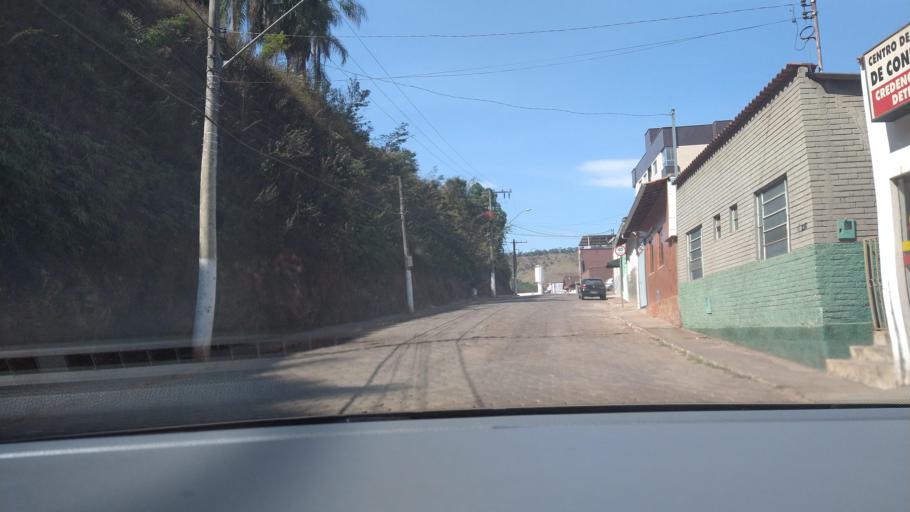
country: BR
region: Minas Gerais
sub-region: Rio Piracicaba
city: Rio Piracicaba
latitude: -19.9282
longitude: -43.1718
